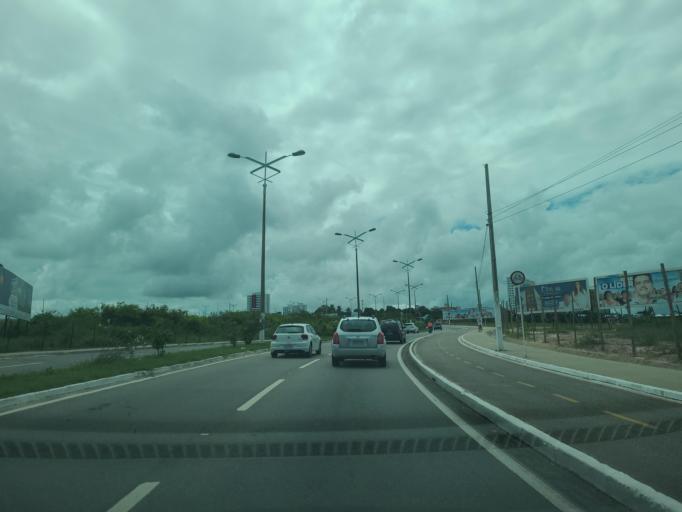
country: BR
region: Alagoas
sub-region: Maceio
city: Maceio
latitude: -9.6269
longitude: -35.7033
